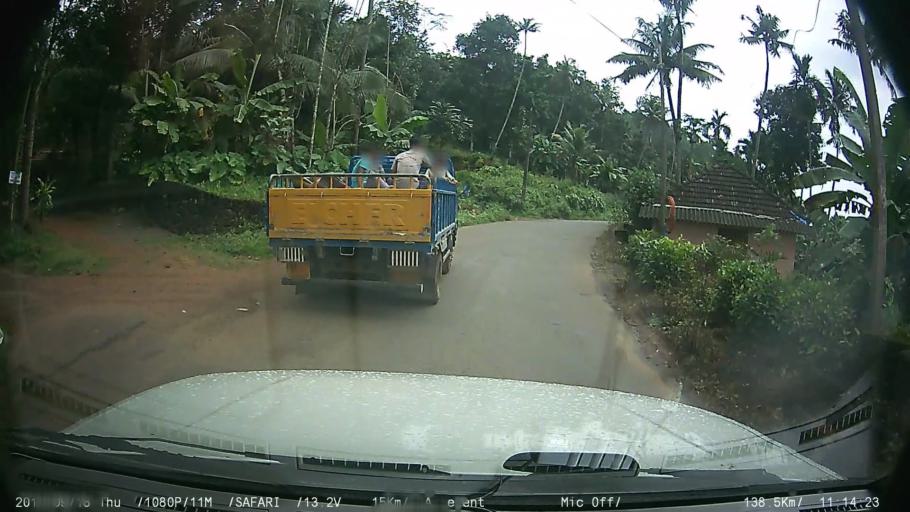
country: IN
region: Kerala
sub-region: Ernakulam
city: Muvattupuzha
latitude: 9.9110
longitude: 76.6061
